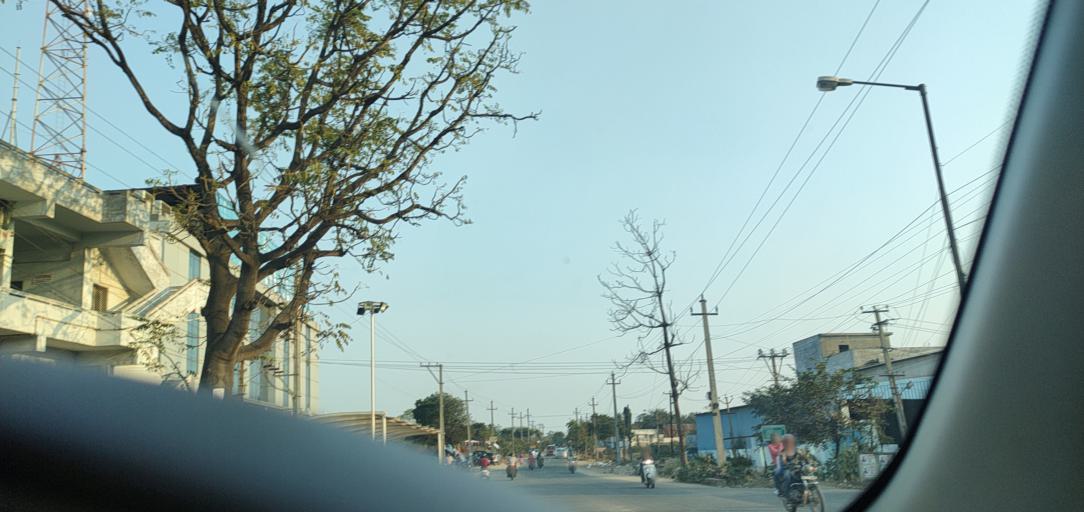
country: IN
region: Telangana
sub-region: Rangareddi
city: Uppal Kalan
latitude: 17.4336
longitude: 78.5774
